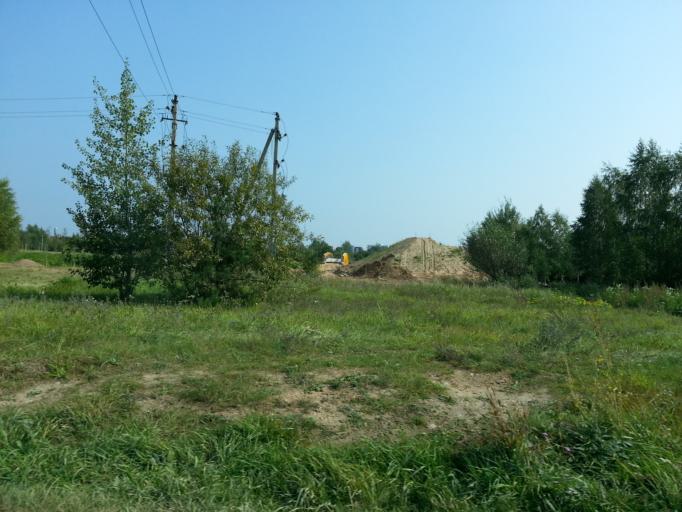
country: LT
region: Vilnius County
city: Pasilaiciai
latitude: 54.7318
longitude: 25.2059
